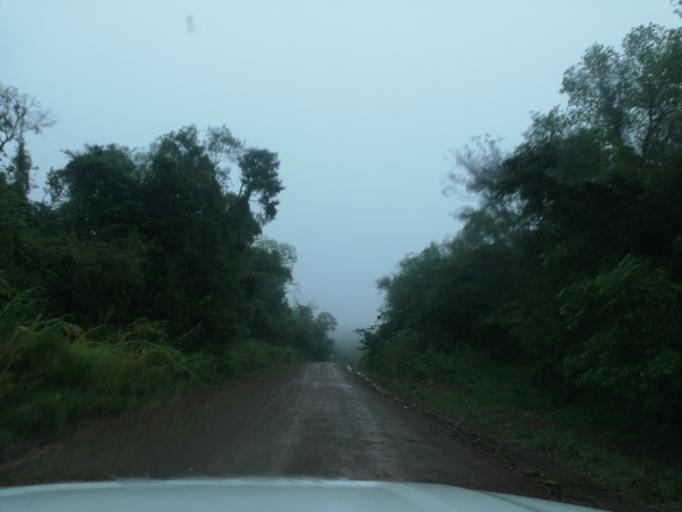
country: AR
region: Misiones
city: Almafuerte
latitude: -27.5114
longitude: -55.3997
